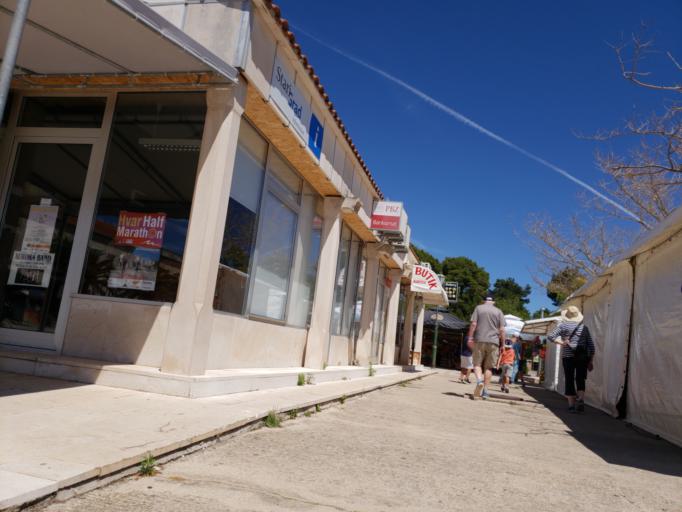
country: HR
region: Splitsko-Dalmatinska
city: Stari Grad
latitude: 43.1846
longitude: 16.5992
